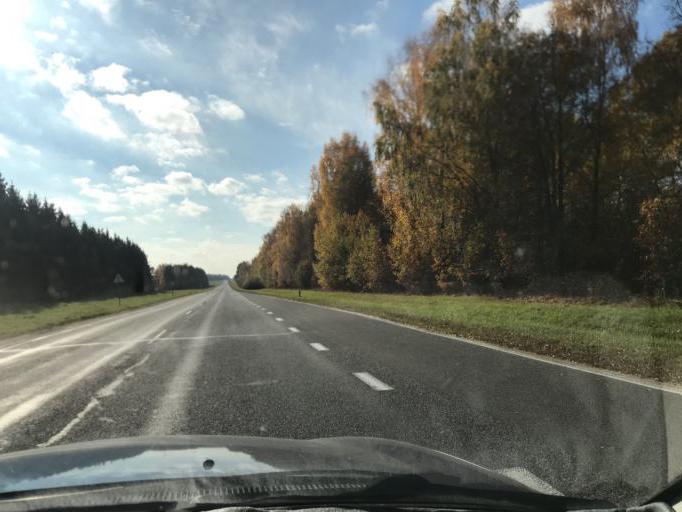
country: BY
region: Grodnenskaya
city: Voranava
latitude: 54.2067
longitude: 25.3499
